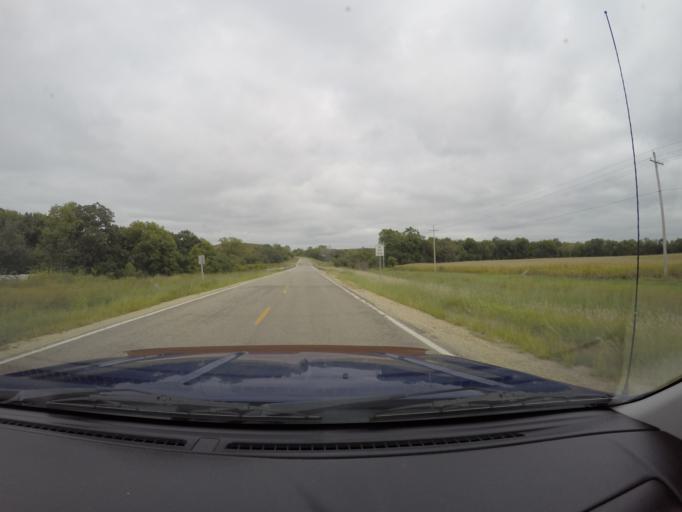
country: US
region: Kansas
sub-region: Dickinson County
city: Herington
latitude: 38.7976
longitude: -96.9416
